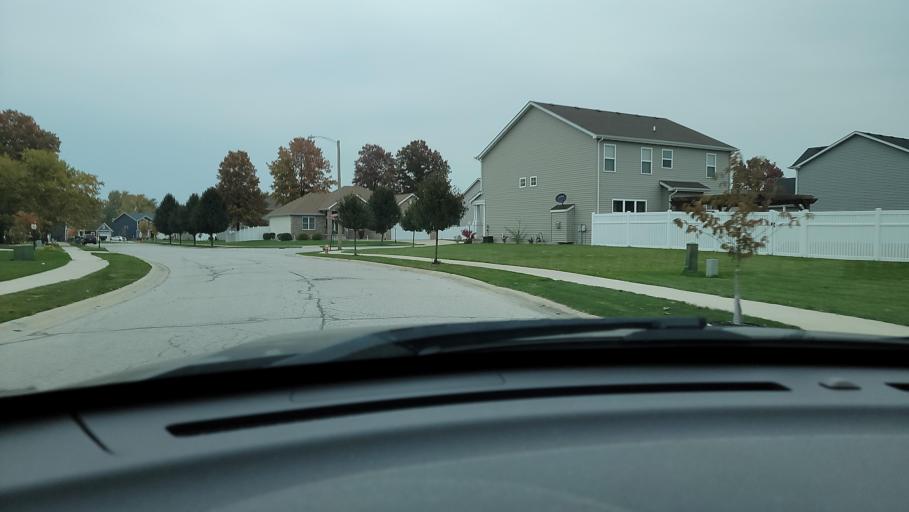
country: US
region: Indiana
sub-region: Porter County
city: Portage
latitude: 41.5678
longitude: -87.1673
